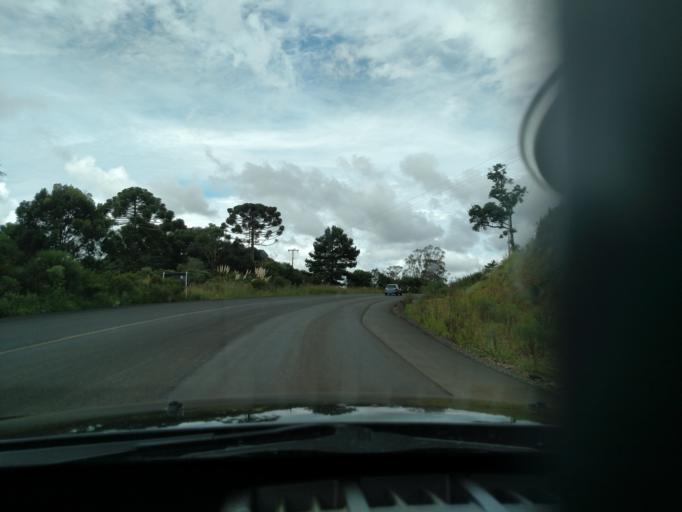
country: BR
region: Santa Catarina
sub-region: Lages
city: Lages
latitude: -27.9178
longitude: -50.6049
